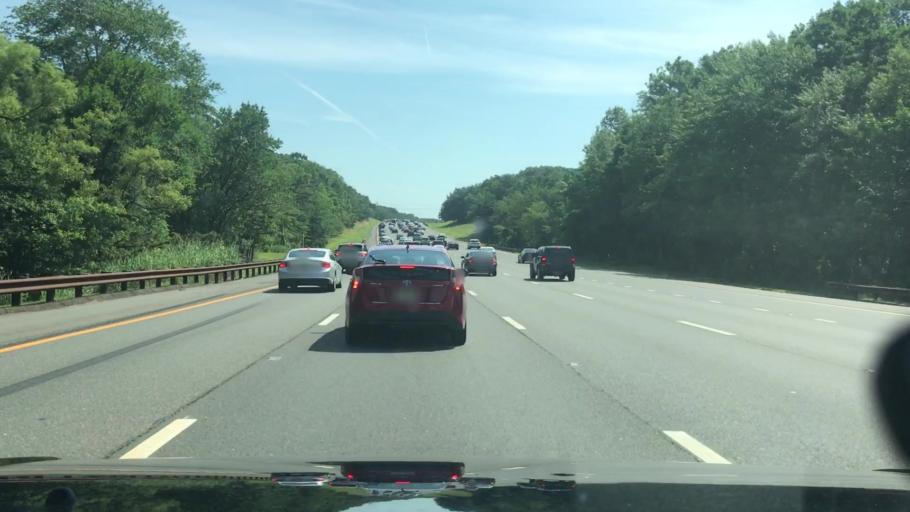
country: US
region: New Jersey
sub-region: Monmouth County
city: Wanamassa
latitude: 40.2455
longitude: -74.0845
